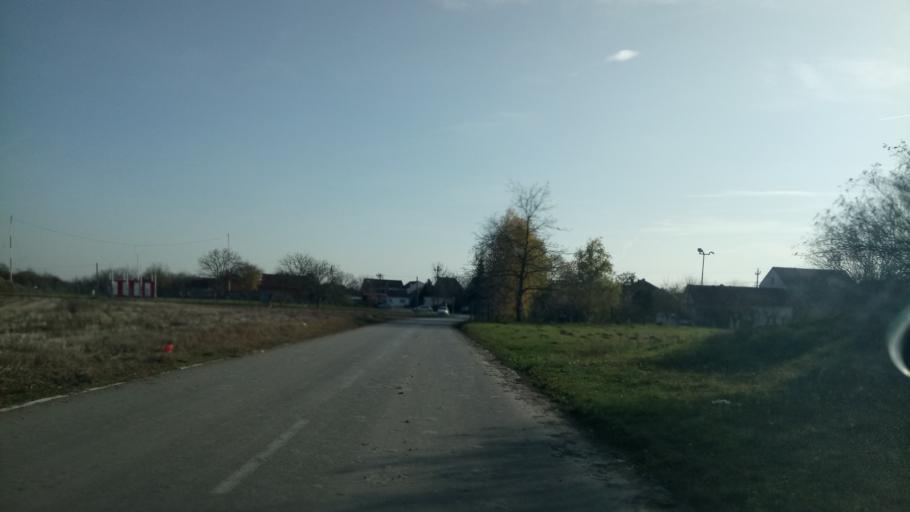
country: RS
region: Autonomna Pokrajina Vojvodina
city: Nova Pazova
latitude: 44.9542
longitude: 20.2252
